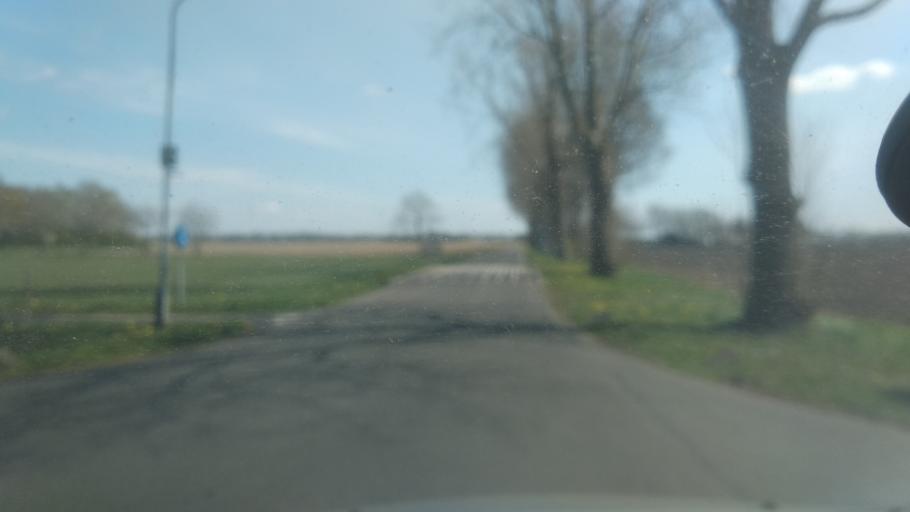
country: NL
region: Groningen
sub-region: Gemeente Stadskanaal
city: Stadskanaal
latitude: 52.9154
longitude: 6.9026
